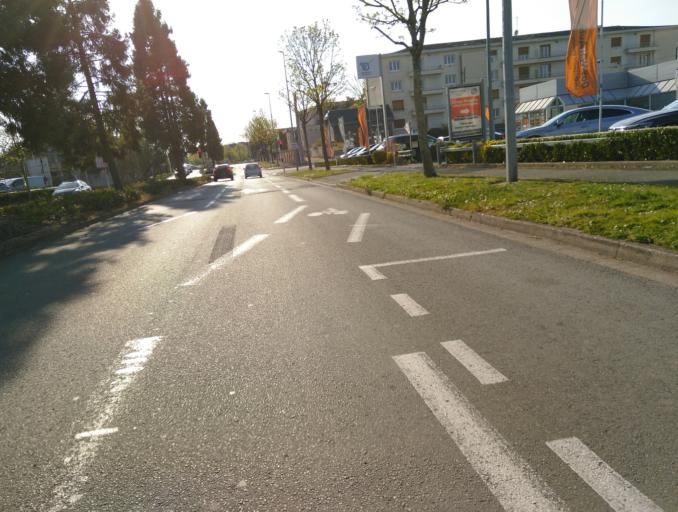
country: FR
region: Pays de la Loire
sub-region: Departement de Maine-et-Loire
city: Angers
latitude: 47.4487
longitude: -0.5357
